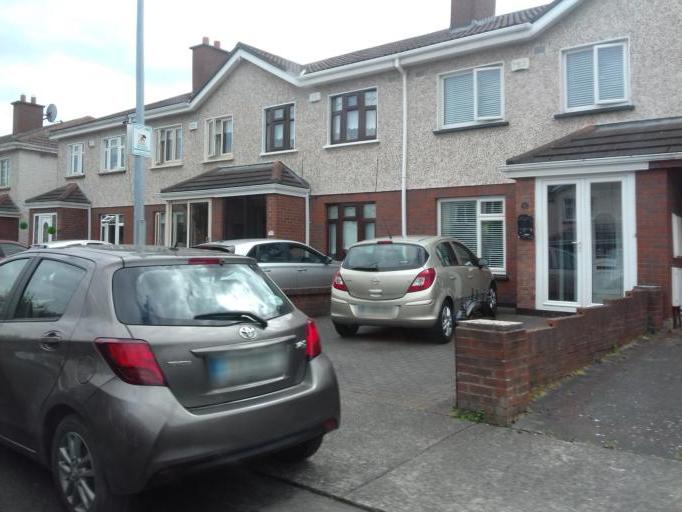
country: IE
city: Greenhills
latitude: 53.3274
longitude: -6.2998
